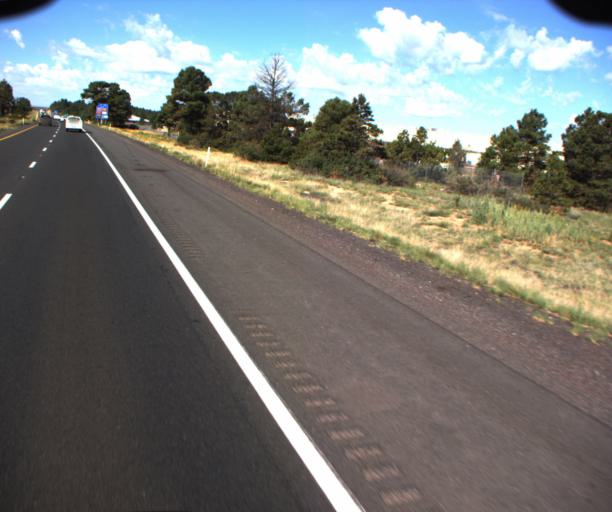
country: US
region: Arizona
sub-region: Coconino County
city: Flagstaff
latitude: 35.2099
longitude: -111.5980
